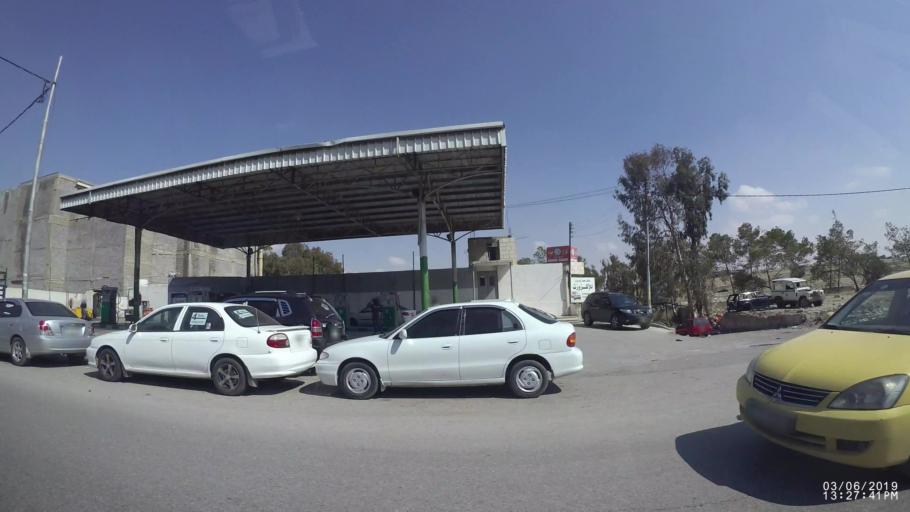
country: JO
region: Zarqa
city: Zarqa
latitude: 32.0704
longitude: 36.0980
